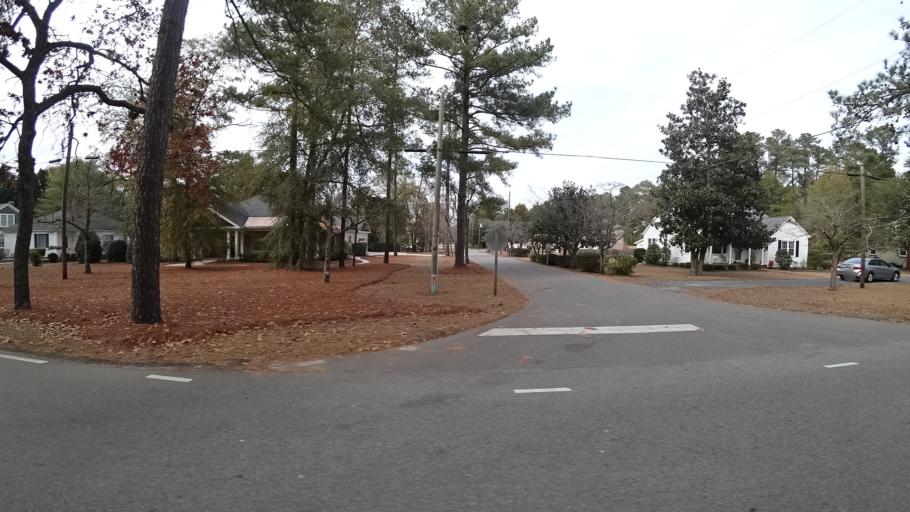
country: US
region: North Carolina
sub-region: Moore County
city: Pinehurst
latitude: 35.2010
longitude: -79.4643
